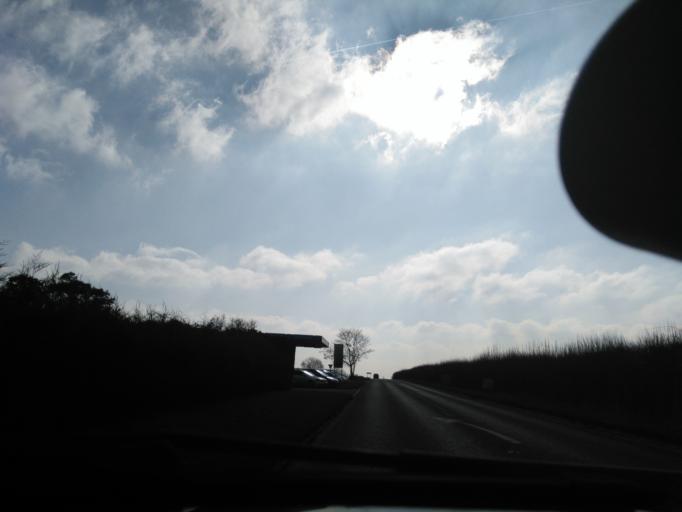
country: GB
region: England
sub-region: Wiltshire
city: Hankerton
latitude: 51.6274
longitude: -2.0754
